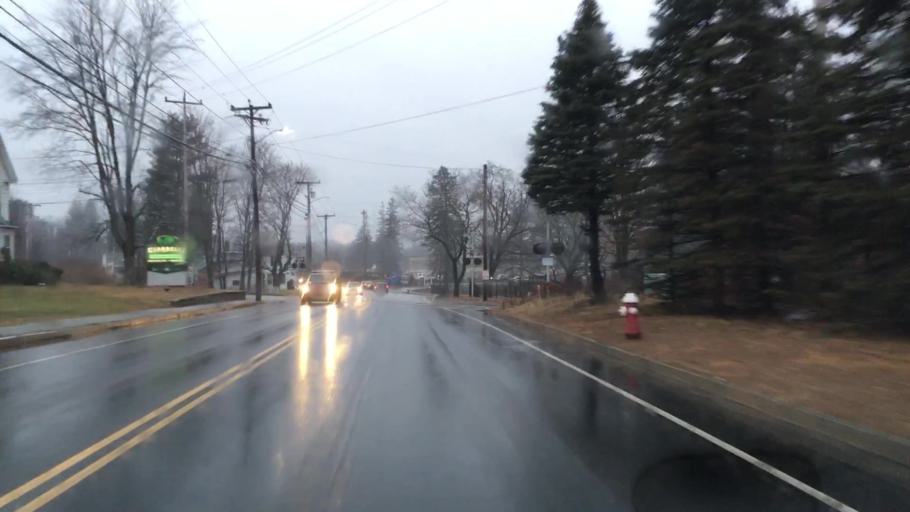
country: US
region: New Hampshire
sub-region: Hillsborough County
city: Milford
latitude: 42.8274
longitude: -71.6320
